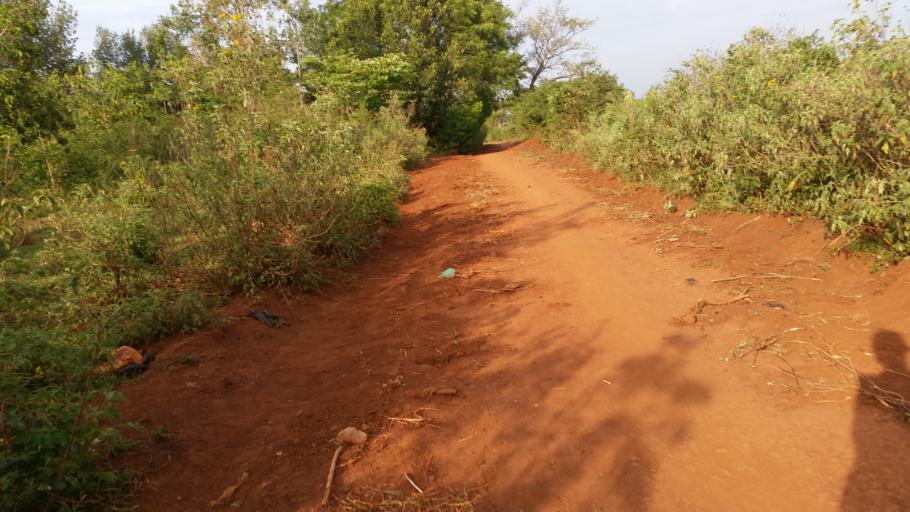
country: UG
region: Eastern Region
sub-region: Busia District
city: Busia
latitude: 0.5365
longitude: 34.0318
